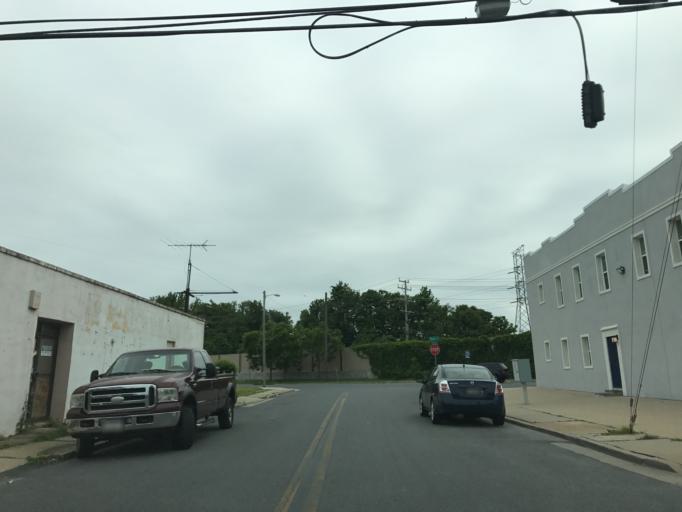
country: US
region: Maryland
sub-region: Baltimore County
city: Dundalk
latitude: 39.2419
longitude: -76.5114
